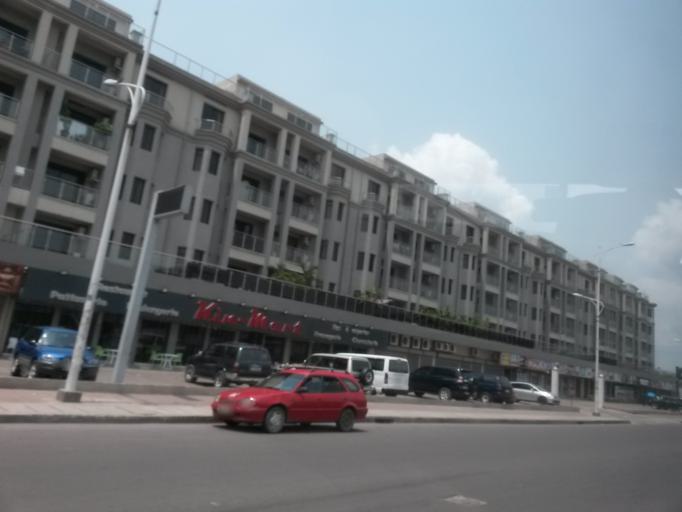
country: CD
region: Kinshasa
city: Kinshasa
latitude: -4.3181
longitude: 15.2931
